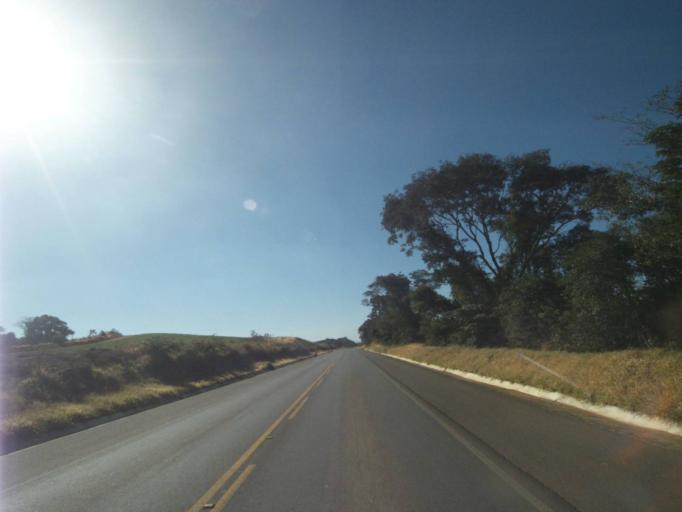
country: BR
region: Parana
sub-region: Tibagi
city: Tibagi
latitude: -24.7321
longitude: -50.4530
